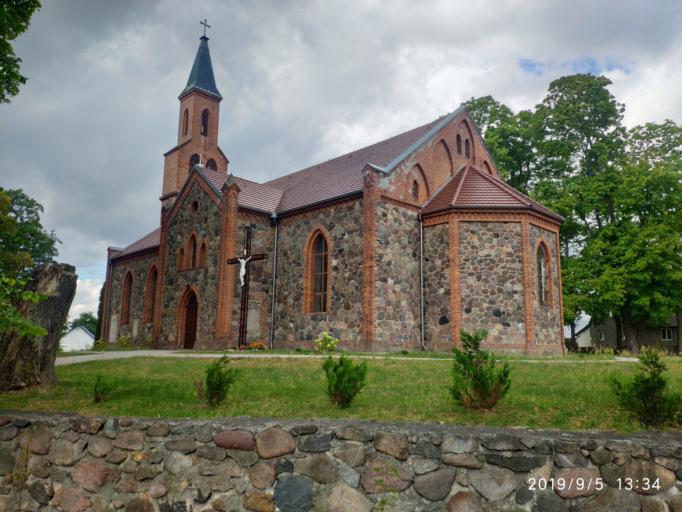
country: PL
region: Lubusz
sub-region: Powiat krosnienski
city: Dabie
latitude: 51.9967
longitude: 15.1994
